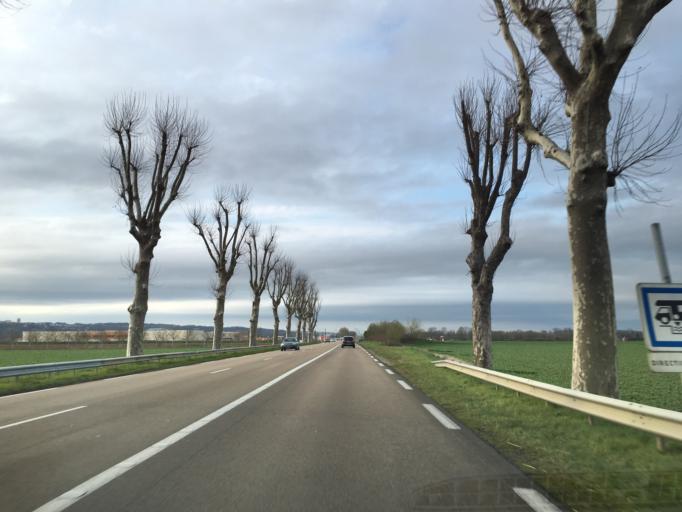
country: FR
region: Bourgogne
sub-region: Departement de l'Yonne
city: Maillot
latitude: 48.1677
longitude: 3.2981
